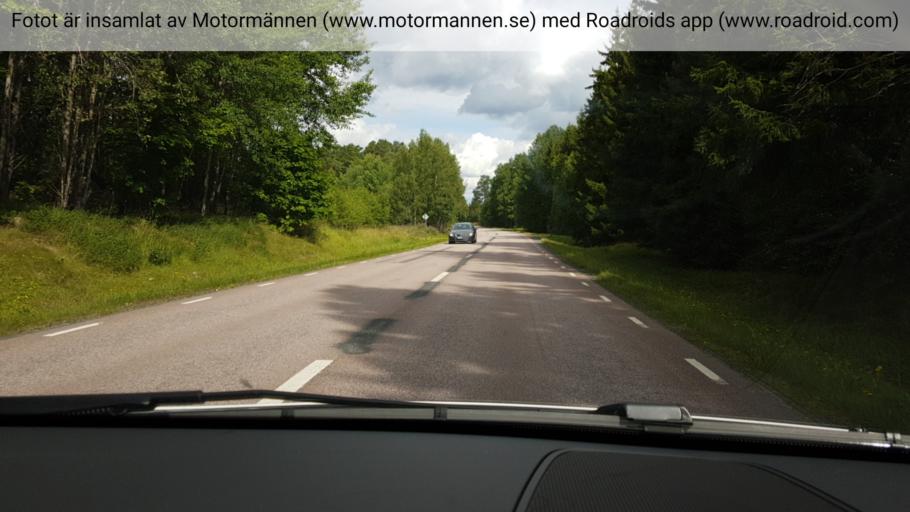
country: SE
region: Stockholm
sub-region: Norrtalje Kommun
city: Nykvarn
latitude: 59.8256
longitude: 18.0466
